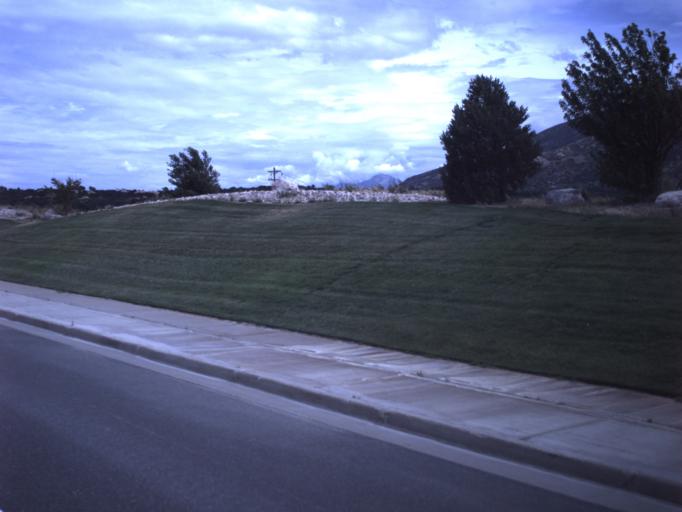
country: US
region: Utah
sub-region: Davis County
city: South Weber
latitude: 41.1283
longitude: -111.9225
